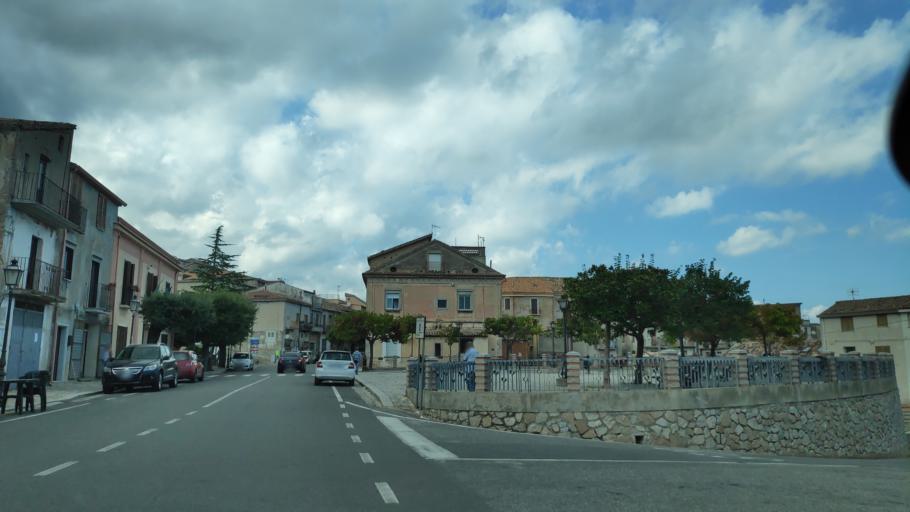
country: IT
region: Calabria
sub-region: Provincia di Catanzaro
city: Santa Caterina dello Ionio
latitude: 38.5332
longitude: 16.5213
